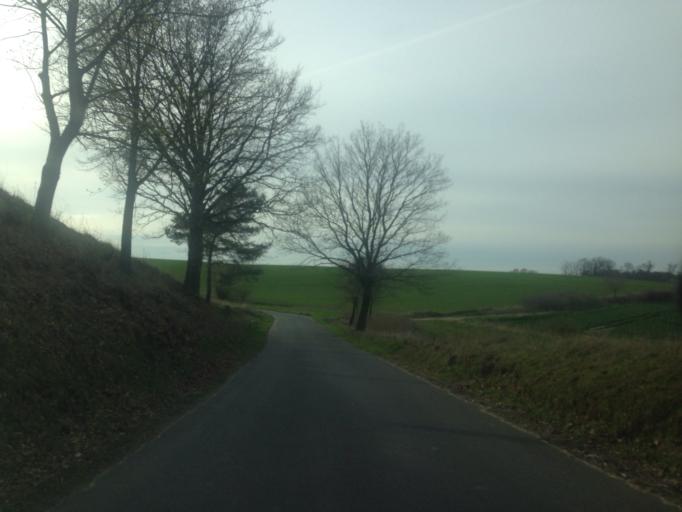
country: PL
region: Kujawsko-Pomorskie
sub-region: Powiat brodnicki
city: Jablonowo Pomorskie
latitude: 53.4507
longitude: 19.1806
